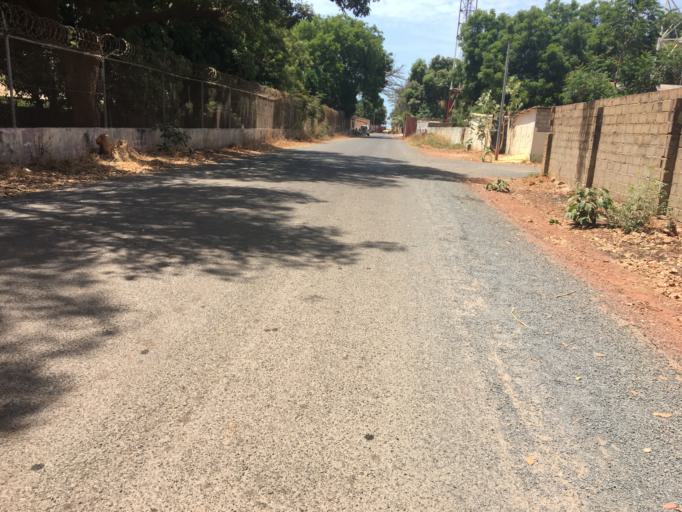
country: GM
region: Banjul
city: Bakau
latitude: 13.4754
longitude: -16.6858
